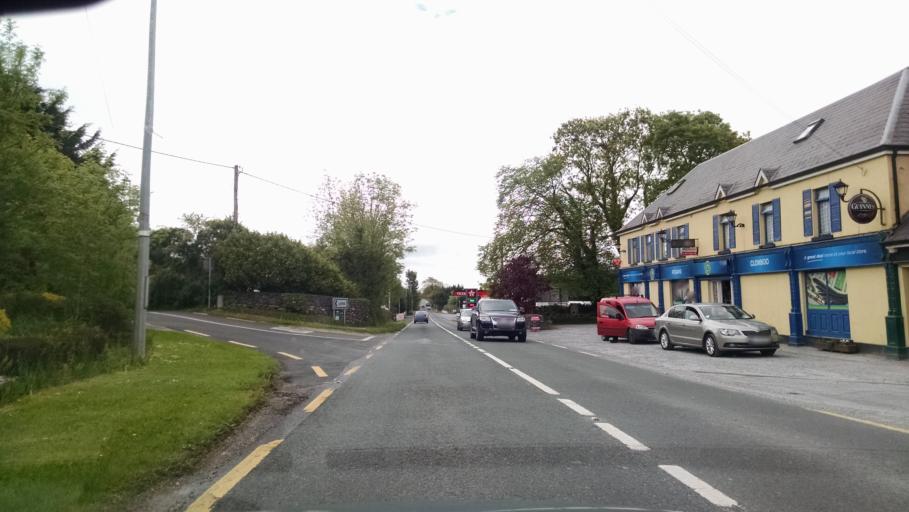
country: IE
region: Connaught
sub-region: County Galway
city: Claregalway
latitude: 53.3756
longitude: -9.0162
